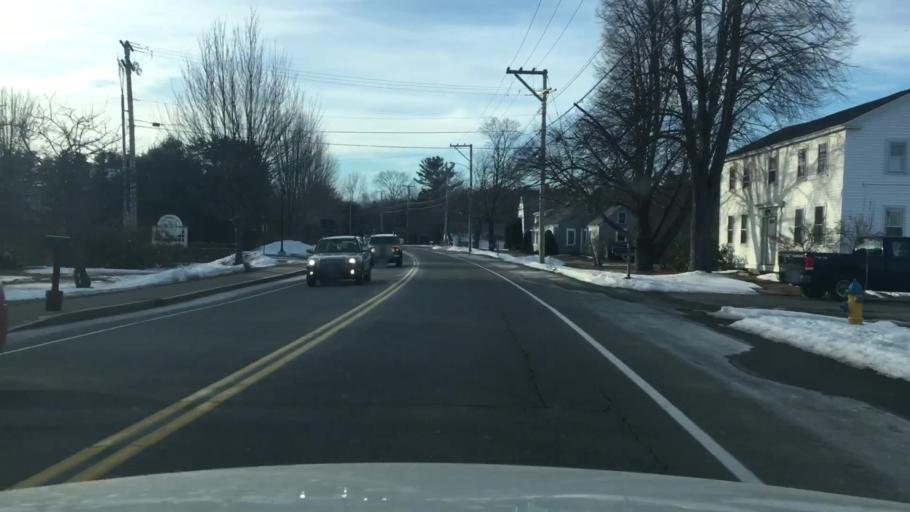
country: US
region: Maine
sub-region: York County
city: Wells Beach Station
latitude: 43.3228
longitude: -70.5844
